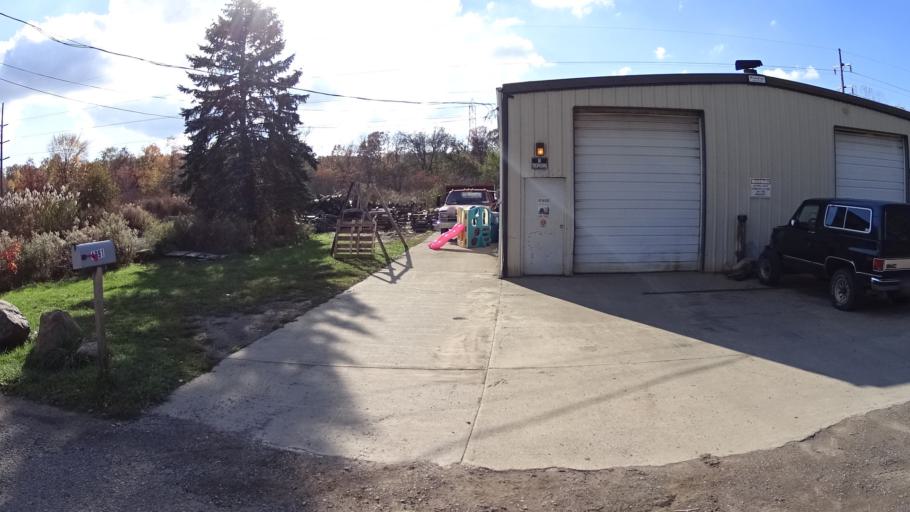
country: US
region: Ohio
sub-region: Lorain County
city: Sheffield
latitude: 41.4262
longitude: -82.1376
